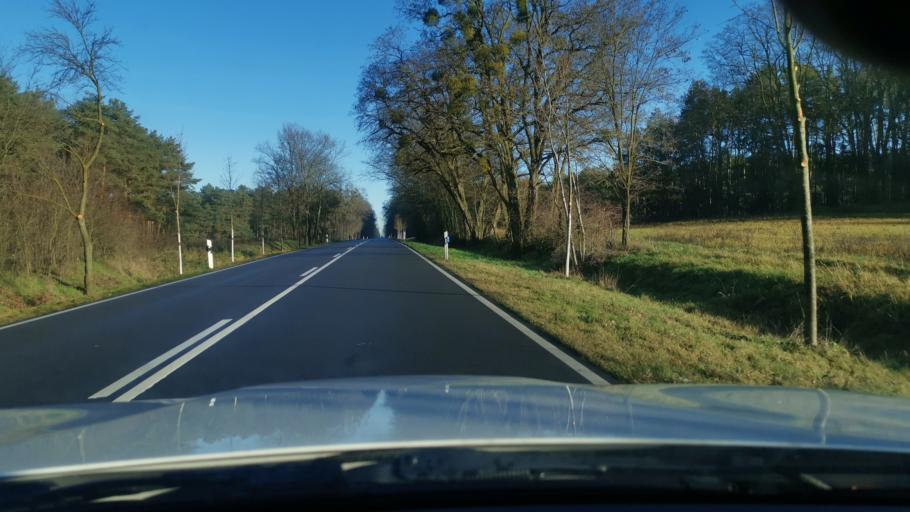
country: DE
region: Saxony-Anhalt
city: Abtsdorf
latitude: 51.9208
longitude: 12.6981
